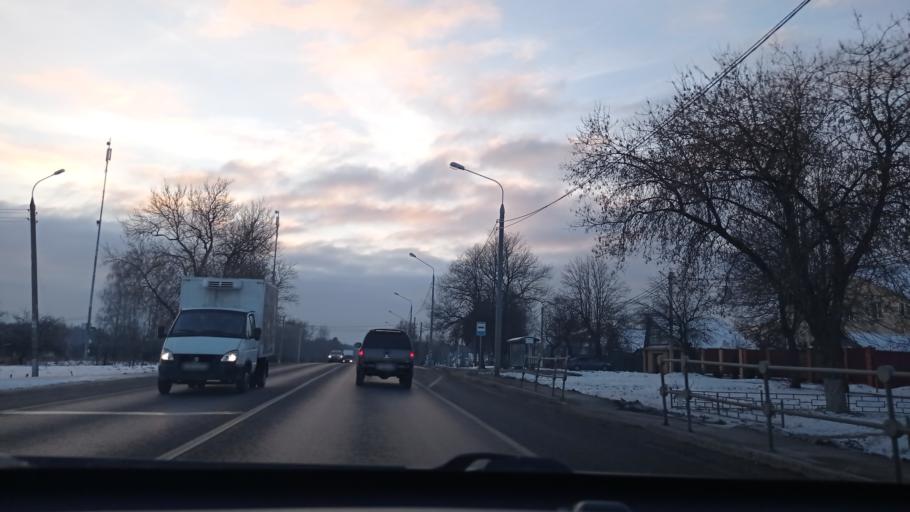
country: RU
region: Moskovskaya
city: Selyatino
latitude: 55.2618
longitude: 37.1026
